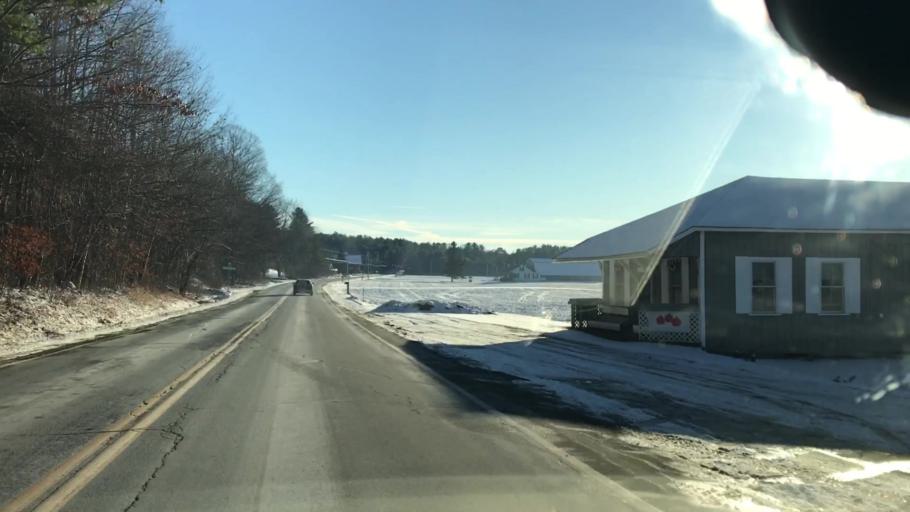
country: US
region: New Hampshire
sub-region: Grafton County
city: Haverhill
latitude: 44.0628
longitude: -72.0486
